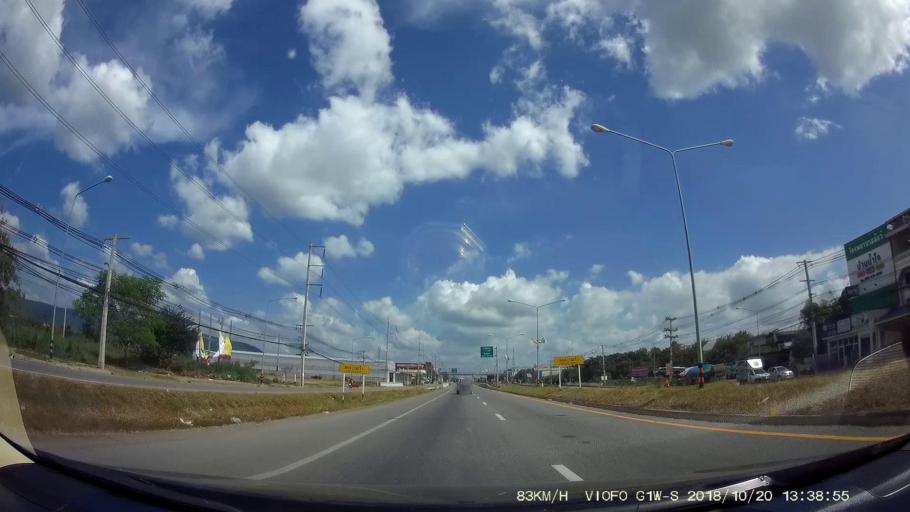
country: TH
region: Khon Kaen
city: Chum Phae
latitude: 16.5505
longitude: 102.0877
